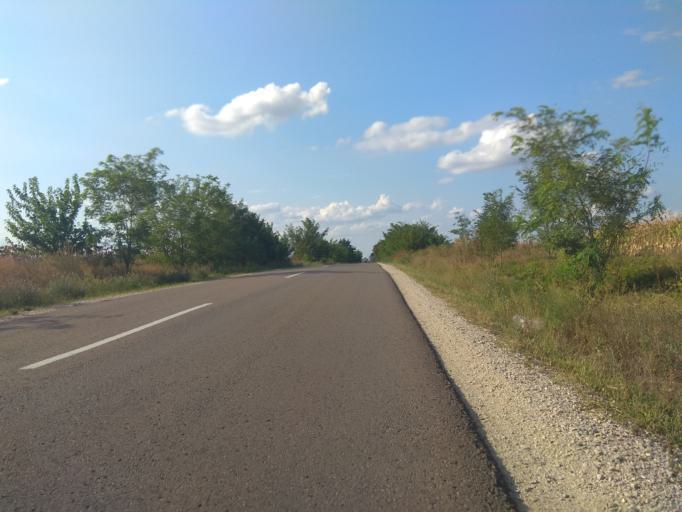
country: HU
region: Borsod-Abauj-Zemplen
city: Hejobaba
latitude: 47.9091
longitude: 20.8860
